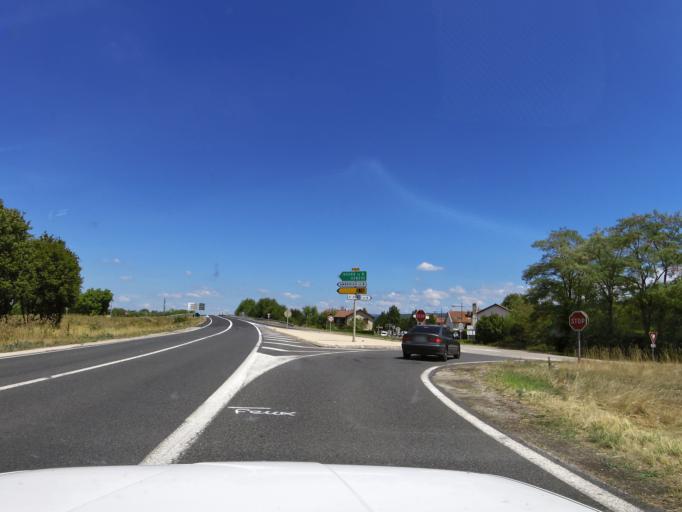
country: FR
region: Rhone-Alpes
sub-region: Departement de l'Ain
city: Saint-Denis-en-Bugey
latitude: 45.9479
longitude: 5.3194
